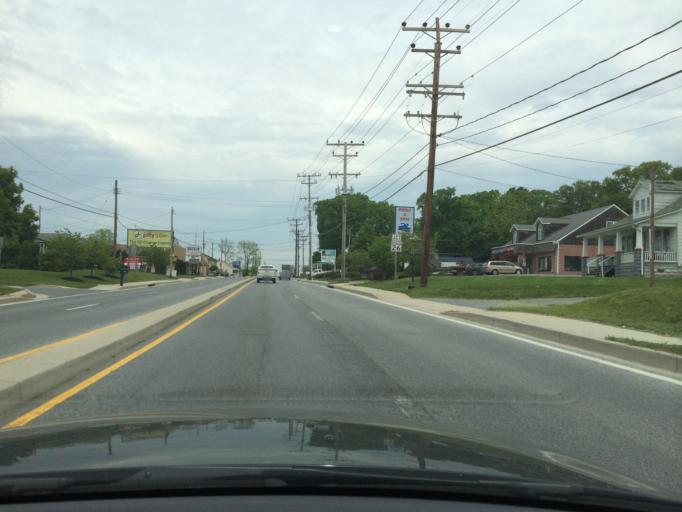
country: US
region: Maryland
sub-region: Carroll County
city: Eldersburg
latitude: 39.4012
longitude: -76.9518
